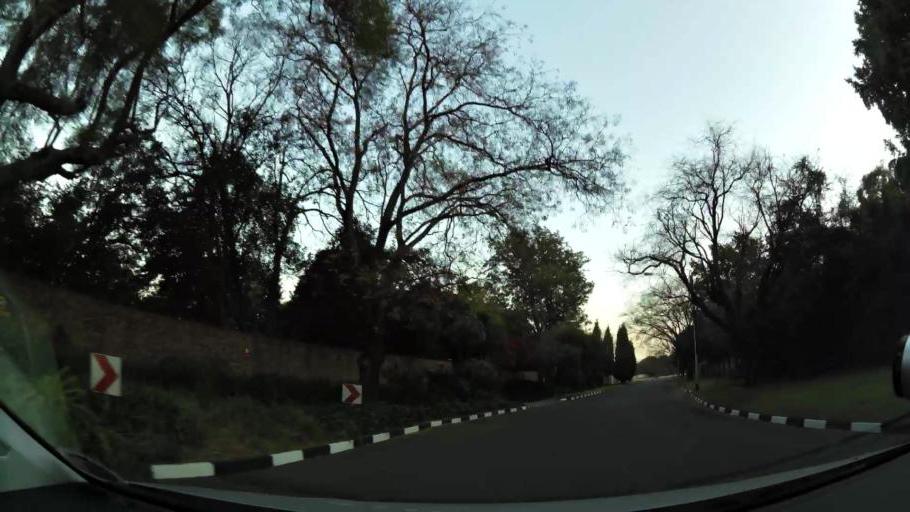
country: ZA
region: Gauteng
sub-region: City of Johannesburg Metropolitan Municipality
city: Johannesburg
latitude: -26.1394
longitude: 28.0562
